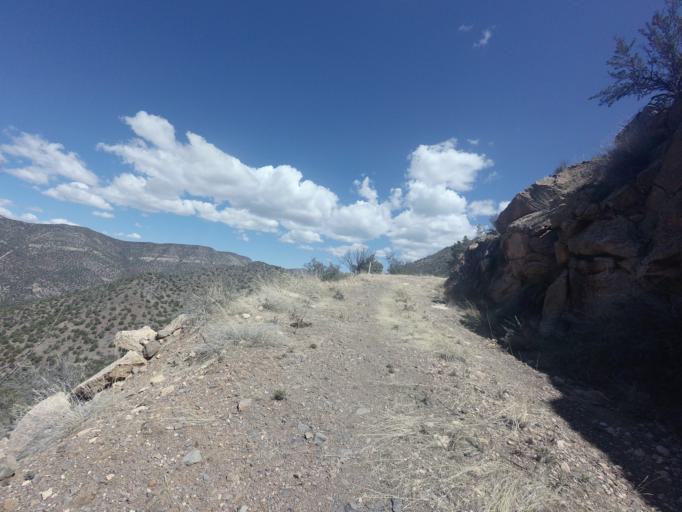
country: US
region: Arizona
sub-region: Gila County
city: Pine
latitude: 34.4025
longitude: -111.6007
